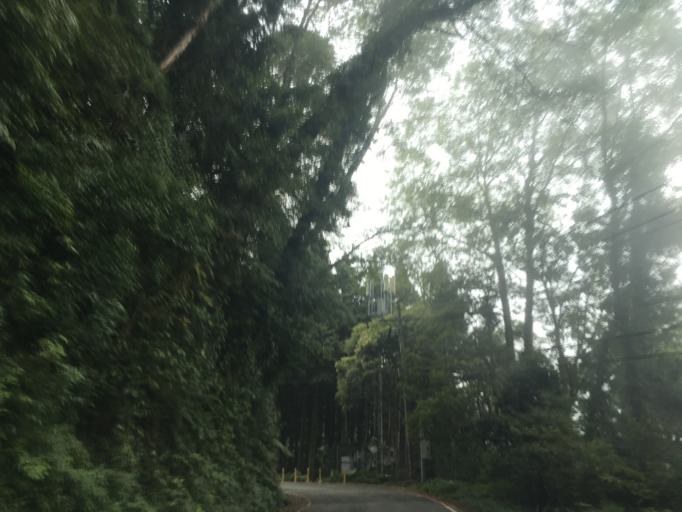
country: TW
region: Taiwan
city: Fengyuan
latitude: 24.2270
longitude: 120.9641
